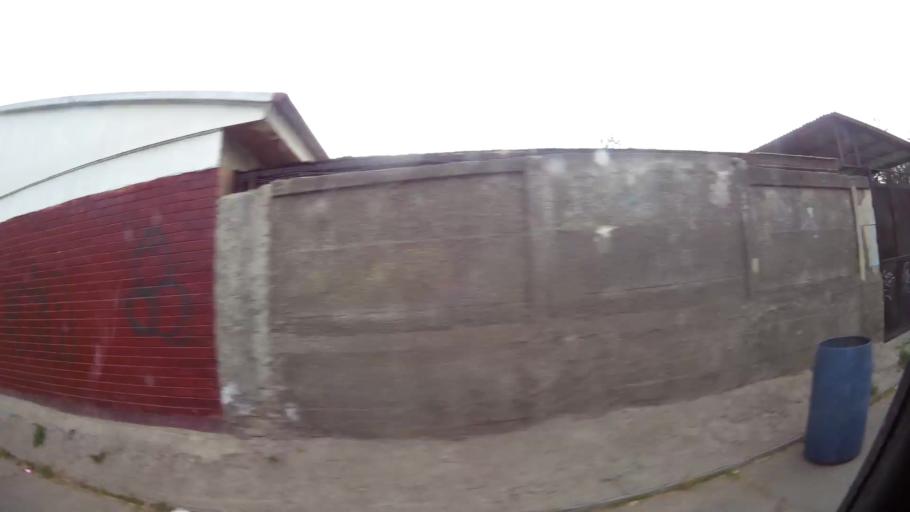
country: CL
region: Santiago Metropolitan
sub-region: Provincia de Santiago
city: Lo Prado
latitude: -33.5183
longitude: -70.7695
